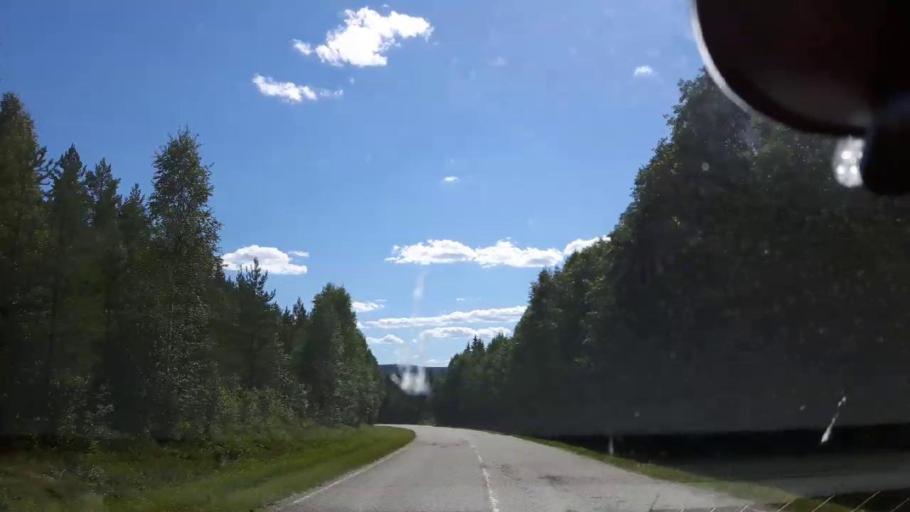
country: SE
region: Vaesternorrland
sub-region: Ange Kommun
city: Fransta
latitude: 62.8020
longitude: 16.2073
